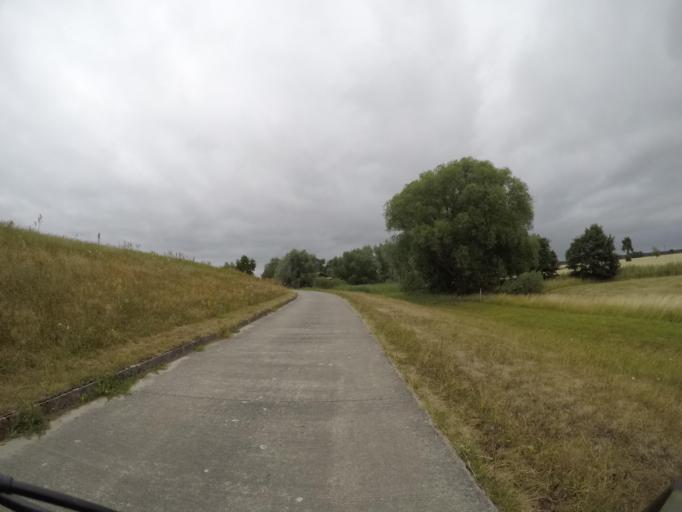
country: DE
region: Lower Saxony
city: Hitzacker
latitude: 53.1589
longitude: 11.0683
